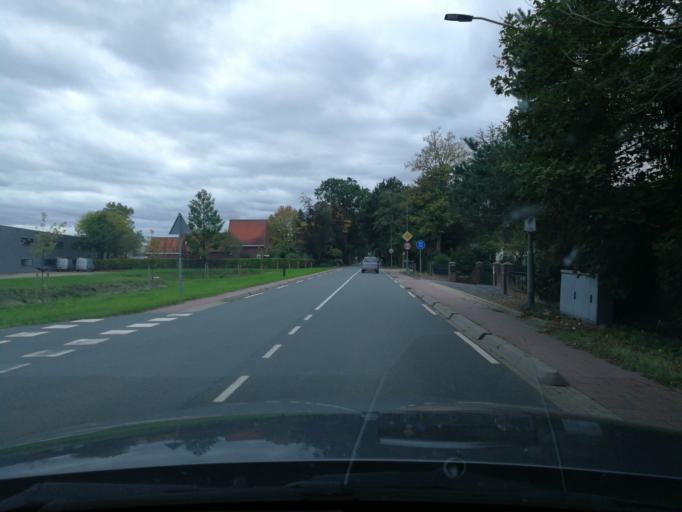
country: NL
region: Limburg
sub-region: Gemeente Venlo
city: Venlo
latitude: 51.3973
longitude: 6.2064
